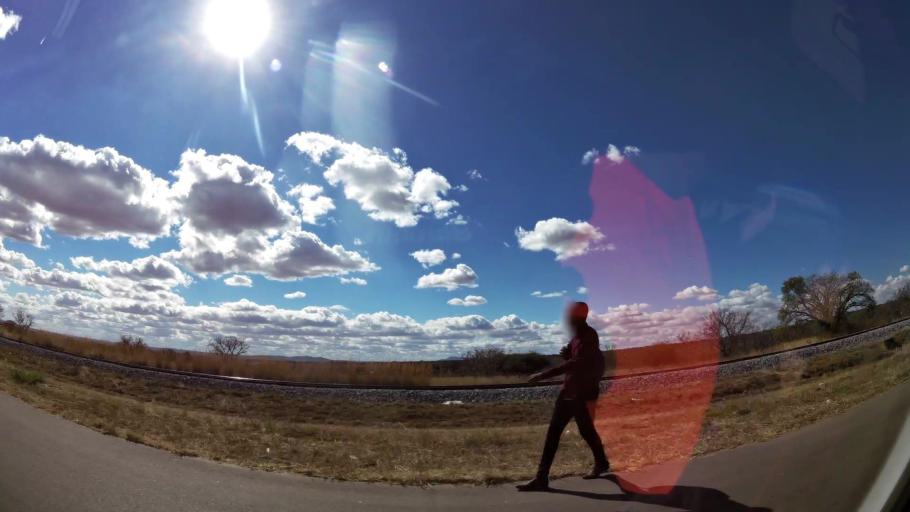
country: ZA
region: Limpopo
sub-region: Capricorn District Municipality
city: Polokwane
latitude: -23.8579
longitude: 29.5087
